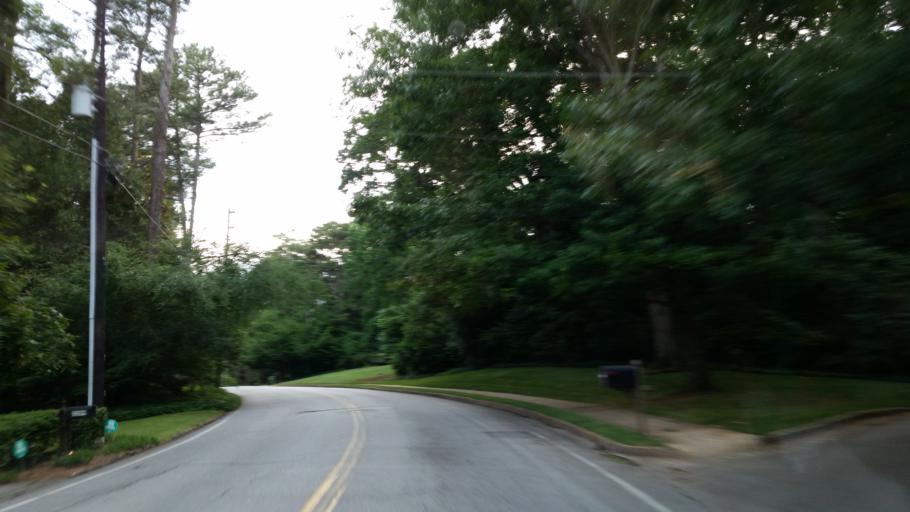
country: US
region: Georgia
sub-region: DeKalb County
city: North Atlanta
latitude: 33.8480
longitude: -84.3918
